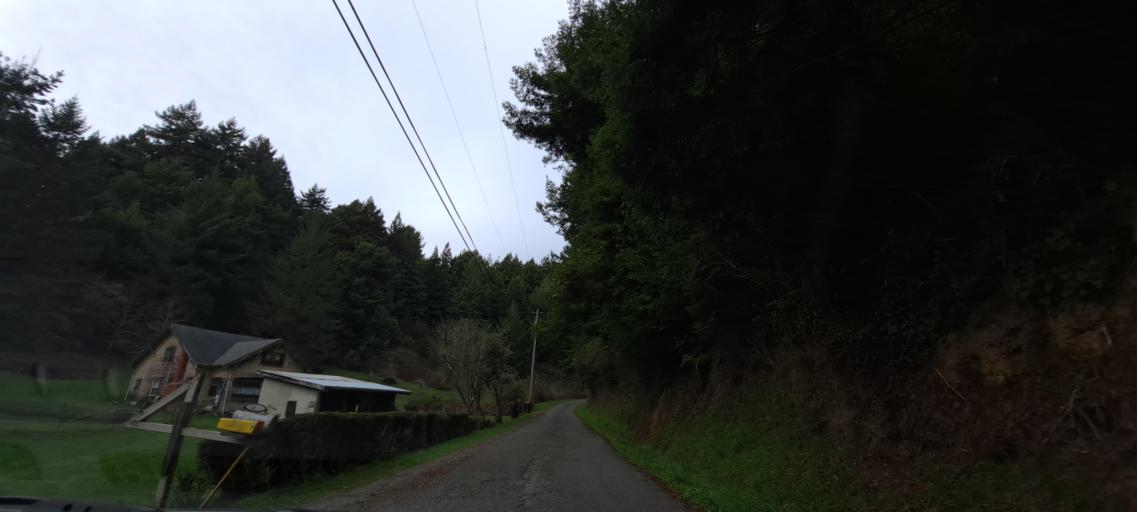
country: US
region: California
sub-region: Humboldt County
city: Fortuna
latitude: 40.6051
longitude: -124.1585
